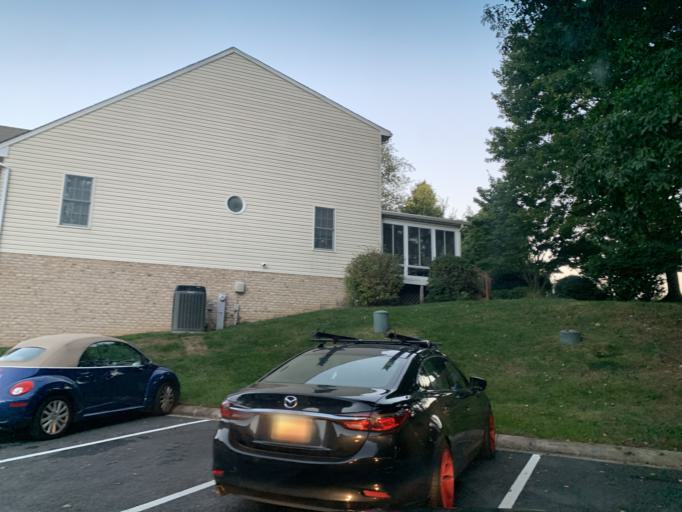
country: US
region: Maryland
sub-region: Harford County
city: Bel Air South
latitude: 39.5248
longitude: -76.3114
